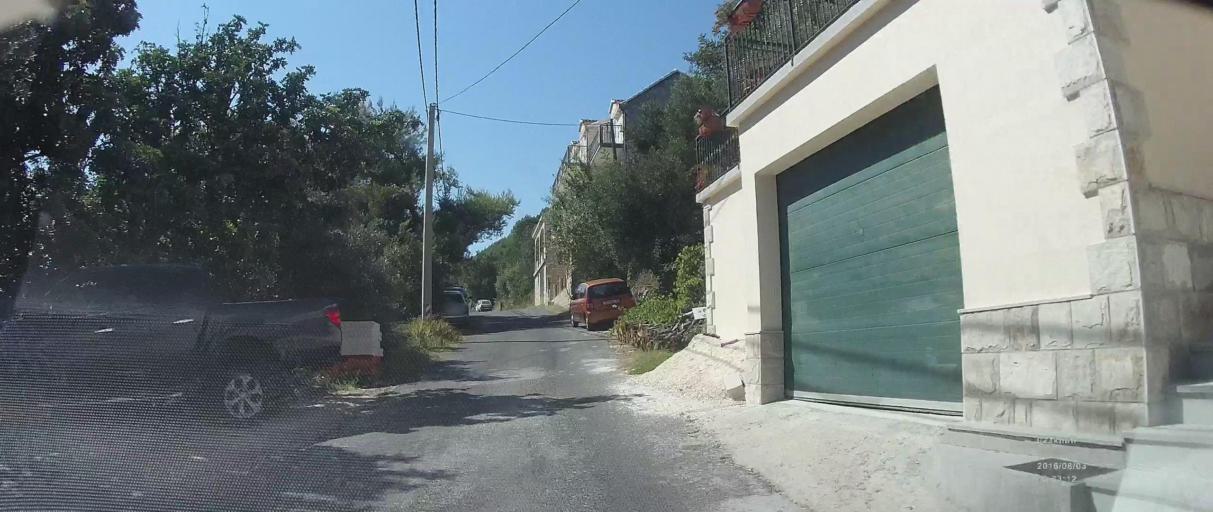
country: HR
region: Dubrovacko-Neretvanska
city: Blato
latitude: 42.7339
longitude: 17.5557
